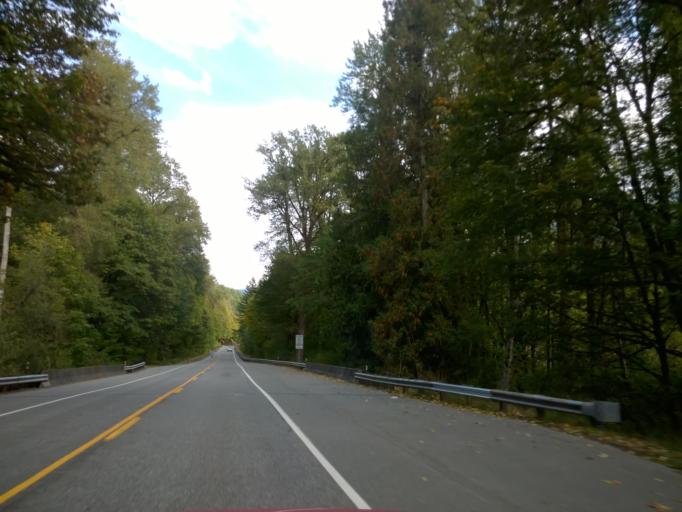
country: US
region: Washington
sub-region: Snohomish County
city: Gold Bar
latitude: 47.7192
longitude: -121.3869
